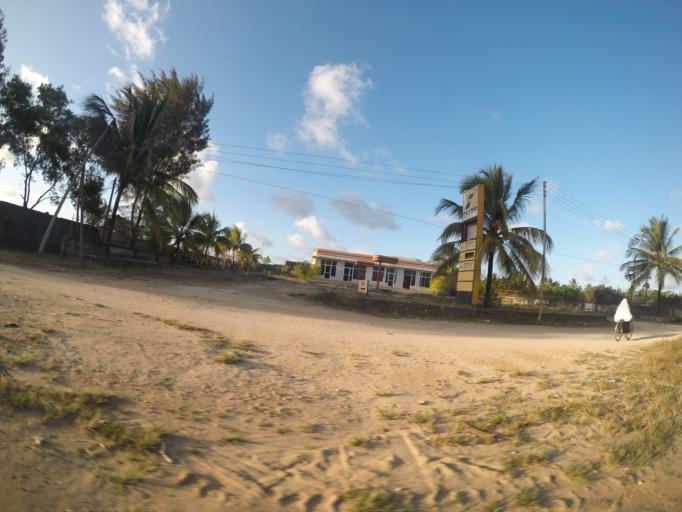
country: TZ
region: Zanzibar Central/South
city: Koani
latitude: -6.2006
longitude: 39.3130
